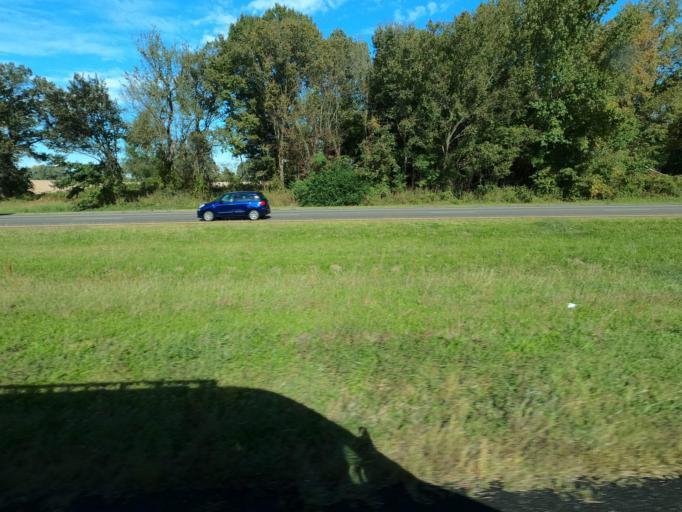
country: US
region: Tennessee
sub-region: Tipton County
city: Mason
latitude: 35.3752
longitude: -89.4579
